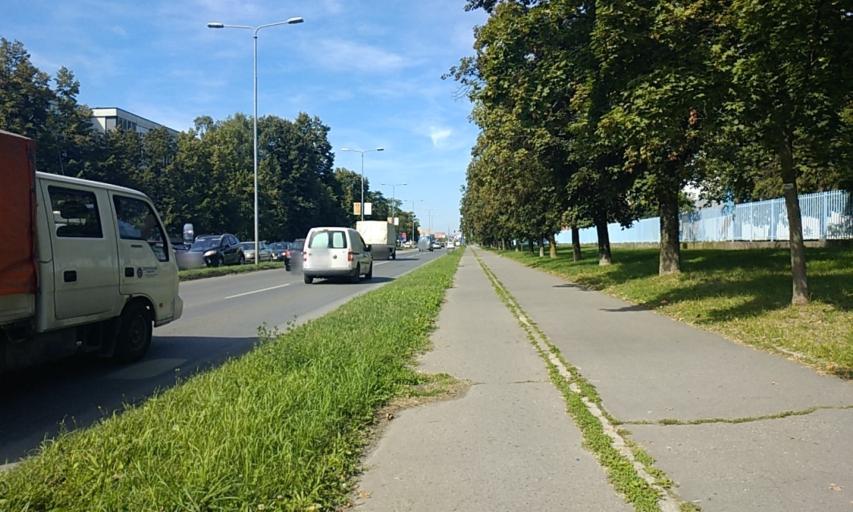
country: BA
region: Republika Srpska
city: Starcevica
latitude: 44.7725
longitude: 17.2090
